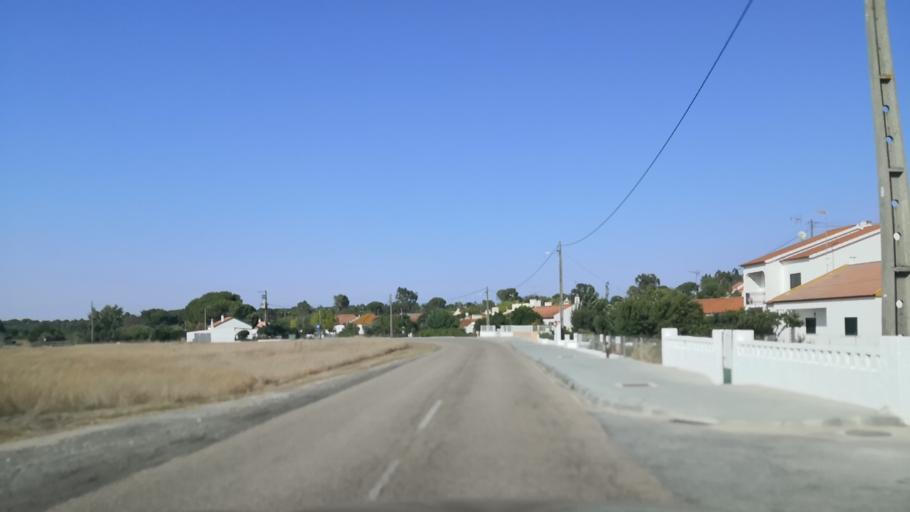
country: PT
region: Santarem
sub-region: Coruche
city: Coruche
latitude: 38.8863
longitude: -8.5357
